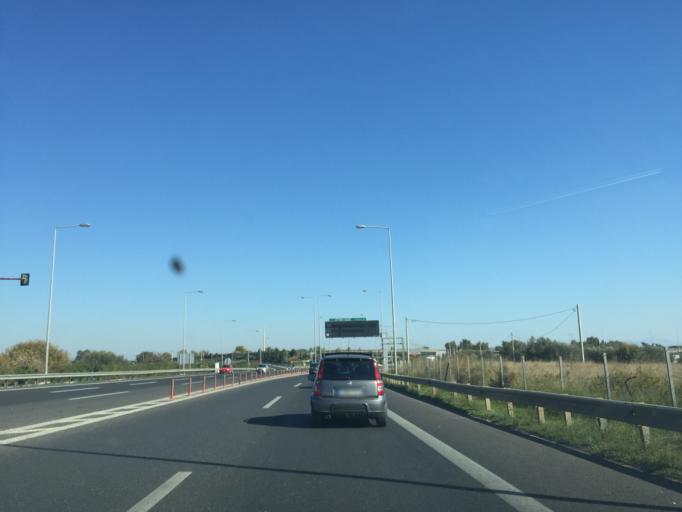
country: GR
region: Attica
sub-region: Nomarchia Anatolikis Attikis
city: Koropi
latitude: 37.9044
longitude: 23.8961
